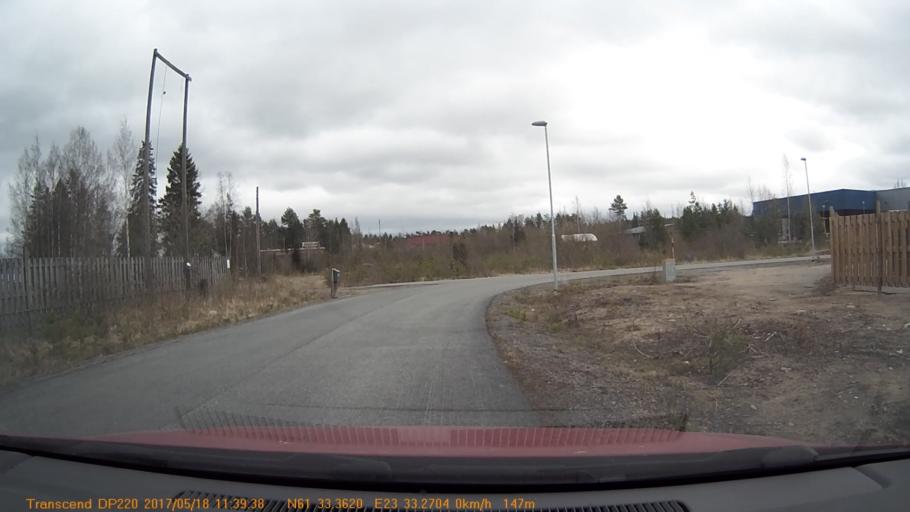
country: FI
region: Pirkanmaa
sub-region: Tampere
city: Yloejaervi
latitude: 61.5560
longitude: 23.5545
